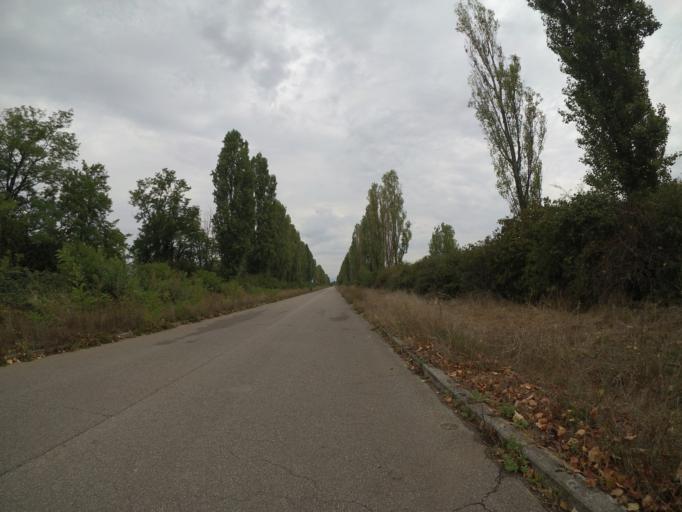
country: IT
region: Friuli Venezia Giulia
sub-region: Provincia di Udine
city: Codroipo
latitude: 45.9593
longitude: 13.0111
